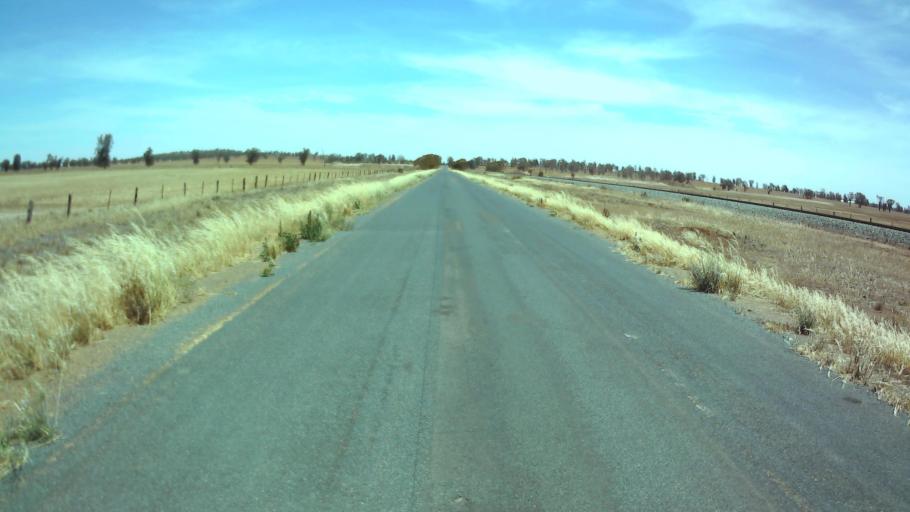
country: AU
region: New South Wales
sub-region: Weddin
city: Grenfell
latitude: -33.7593
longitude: 147.7615
